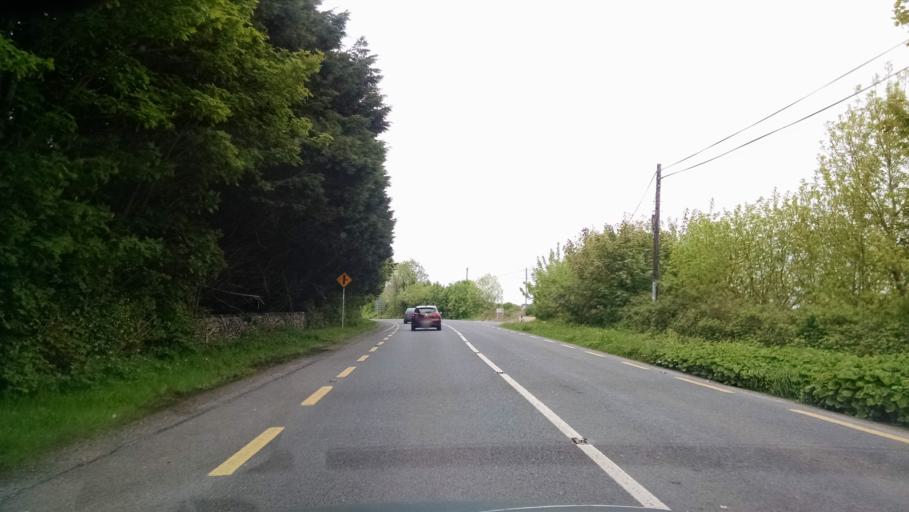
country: IE
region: Connaught
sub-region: County Galway
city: Moycullen
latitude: 53.4801
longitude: -9.0910
